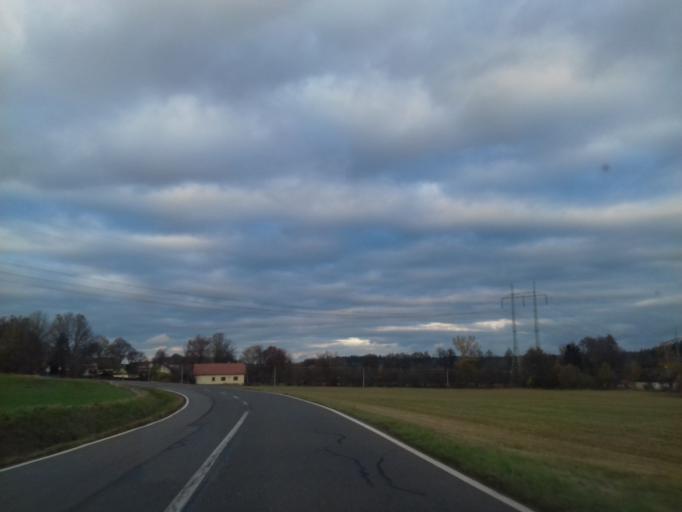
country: CZ
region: Pardubicky
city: Krouna
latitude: 49.7827
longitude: 16.0317
